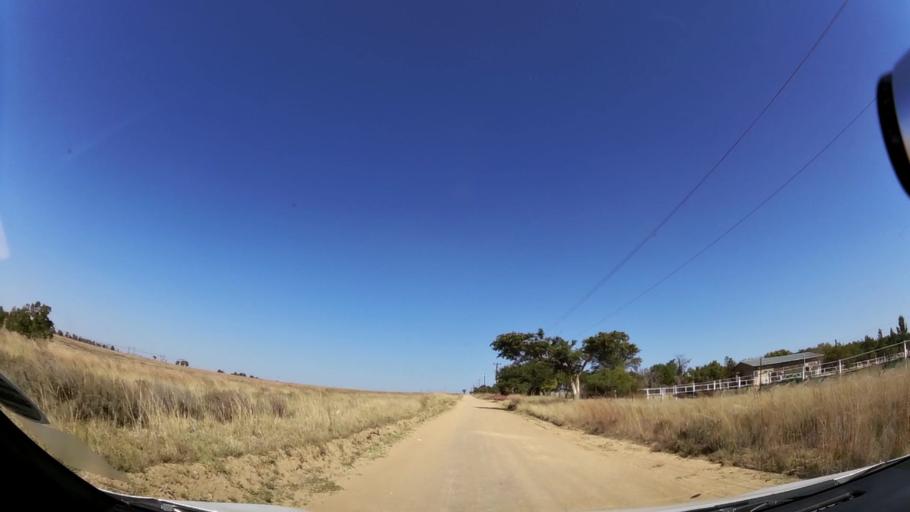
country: ZA
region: Gauteng
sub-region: City of Johannesburg Metropolitan Municipality
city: Diepsloot
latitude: -25.9104
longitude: 28.0706
